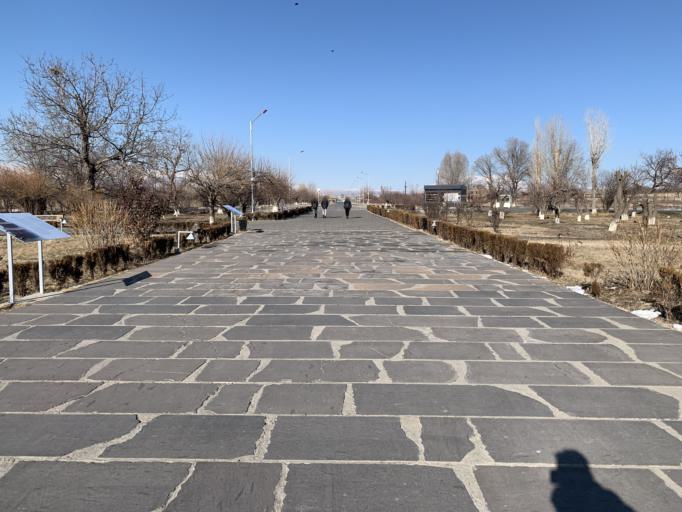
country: AM
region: Armavir
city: Voskehat
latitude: 40.1607
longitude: 44.3367
